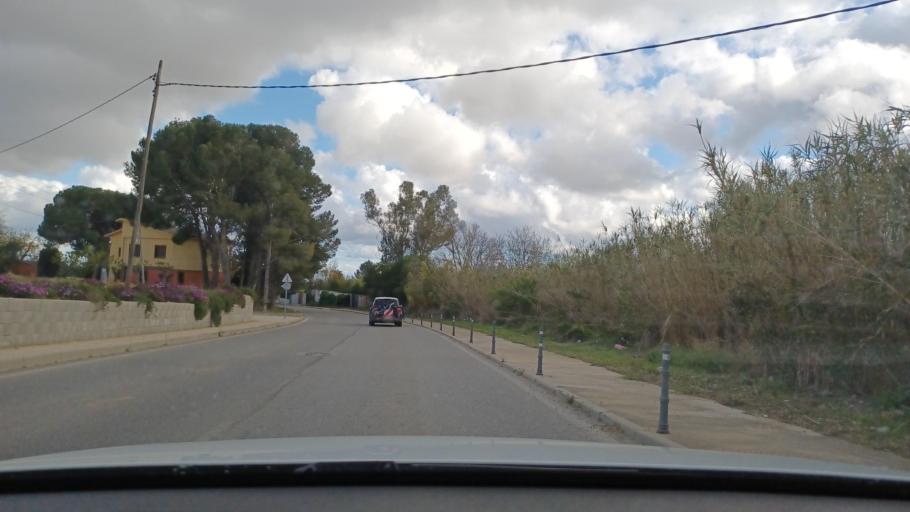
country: ES
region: Catalonia
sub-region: Provincia de Tarragona
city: Botarell
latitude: 41.1356
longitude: 0.9920
